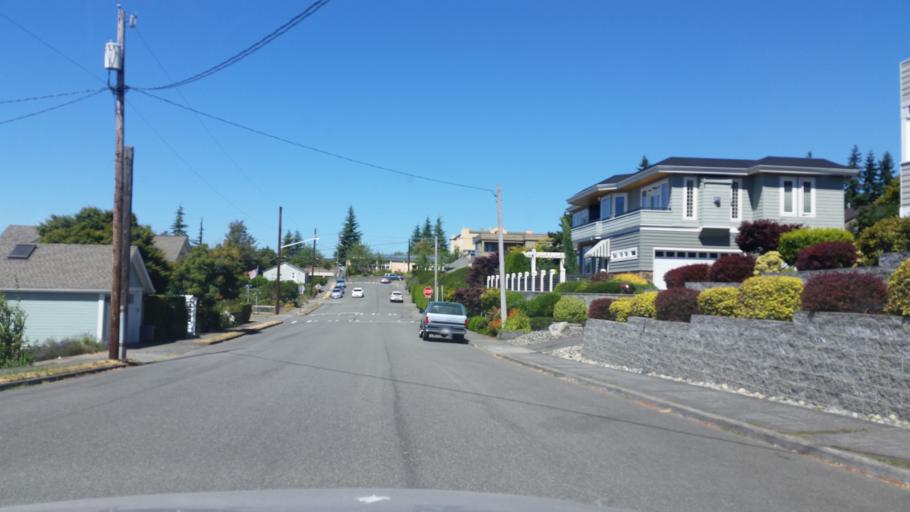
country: US
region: Washington
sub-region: Snohomish County
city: Edmonds
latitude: 47.8082
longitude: -122.3722
